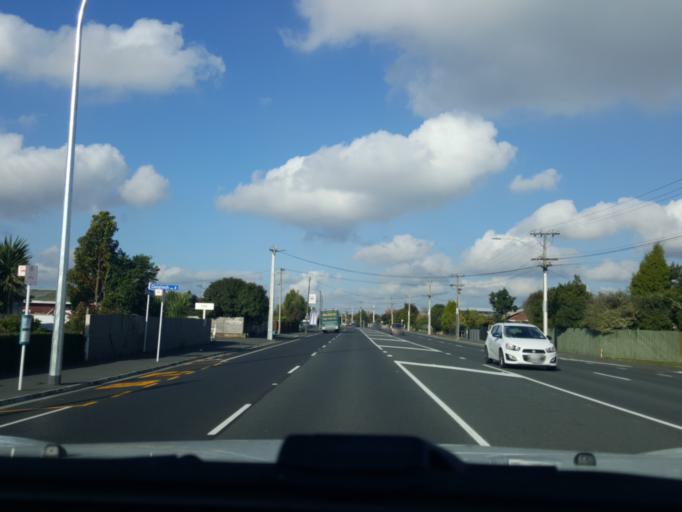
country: NZ
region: Waikato
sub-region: Hamilton City
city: Hamilton
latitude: -37.7661
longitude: 175.2558
